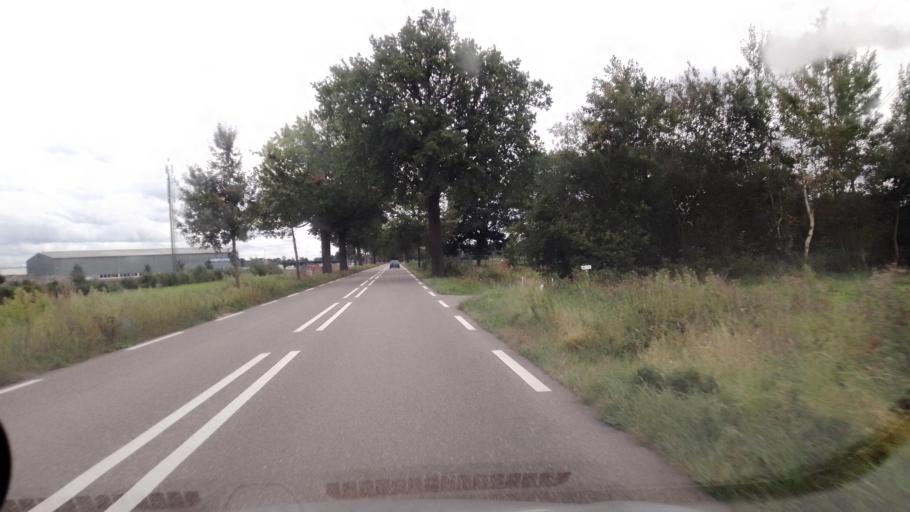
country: NL
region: Limburg
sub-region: Gemeente Peel en Maas
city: Maasbree
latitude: 51.4260
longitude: 6.1002
